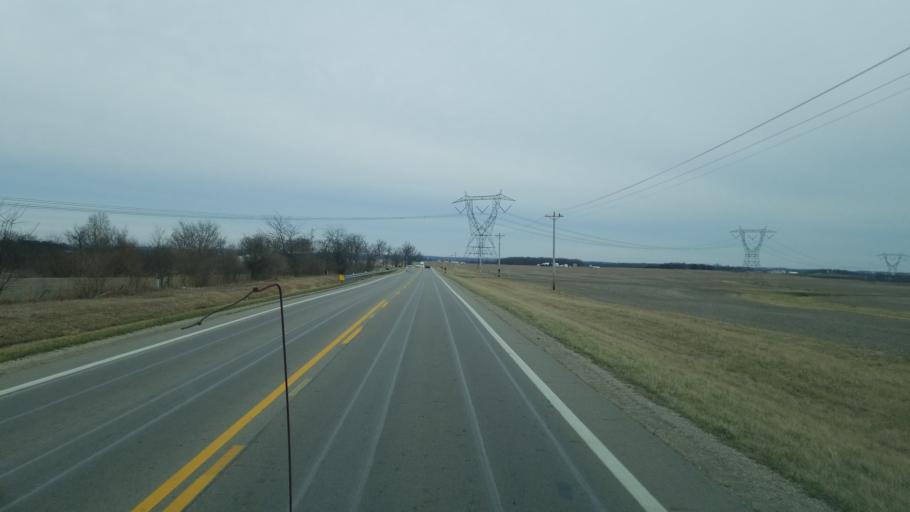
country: US
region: Ohio
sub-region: Pickaway County
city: Logan Elm Village
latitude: 39.5877
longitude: -83.0302
